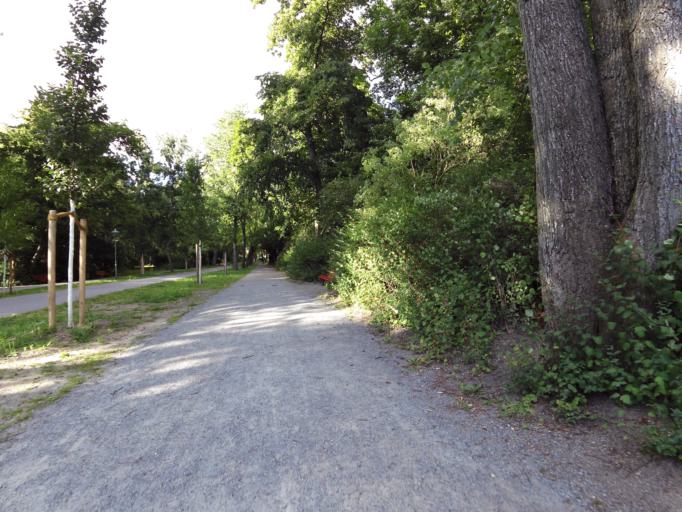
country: DE
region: Berlin
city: Steglitz Bezirk
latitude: 52.4487
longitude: 13.3358
